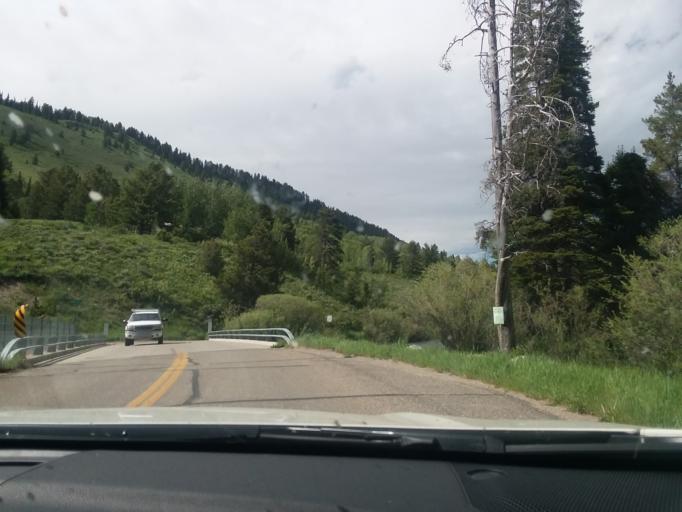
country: US
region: Wyoming
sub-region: Teton County
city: Moose Wilson Road
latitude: 43.5210
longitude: -110.8646
